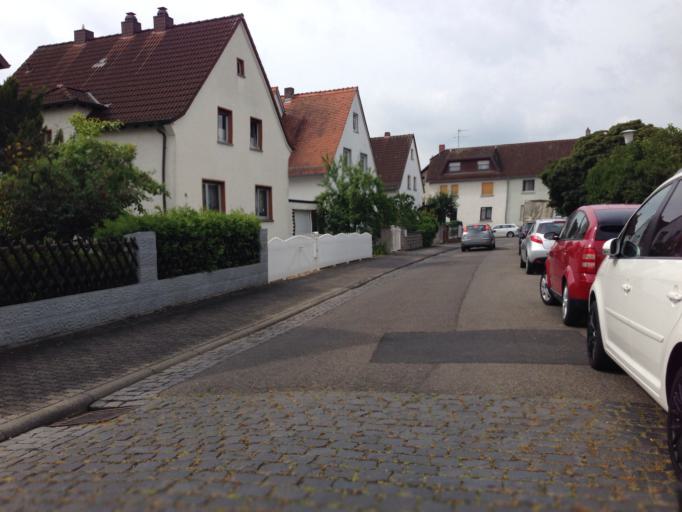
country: DE
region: Hesse
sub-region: Regierungsbezirk Darmstadt
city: Grosskrotzenburg
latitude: 50.0988
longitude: 8.9477
